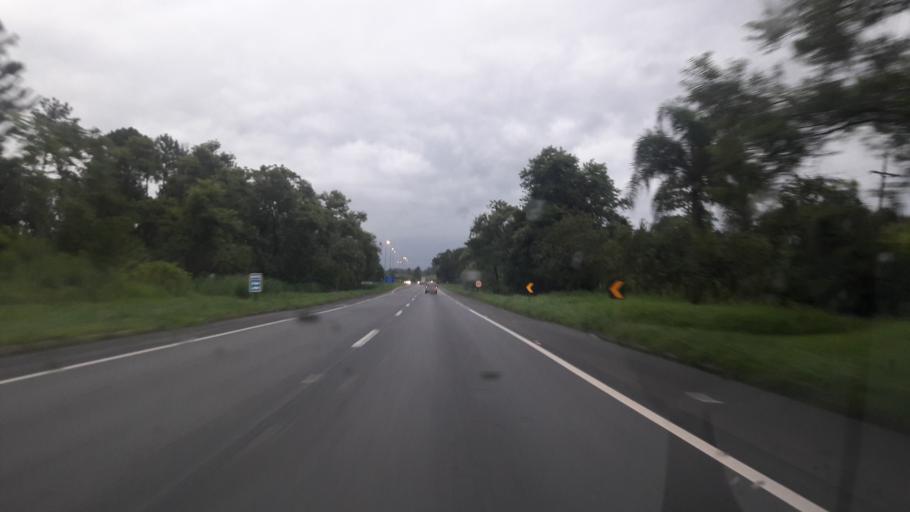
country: BR
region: Sao Paulo
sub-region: Cajati
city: Cajati
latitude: -24.7788
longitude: -48.1705
